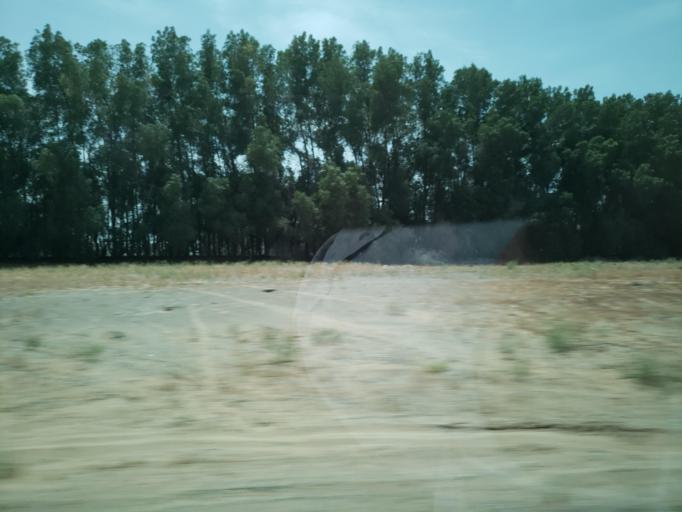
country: AE
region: Ash Shariqah
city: Sharjah
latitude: 25.3206
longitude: 55.5094
